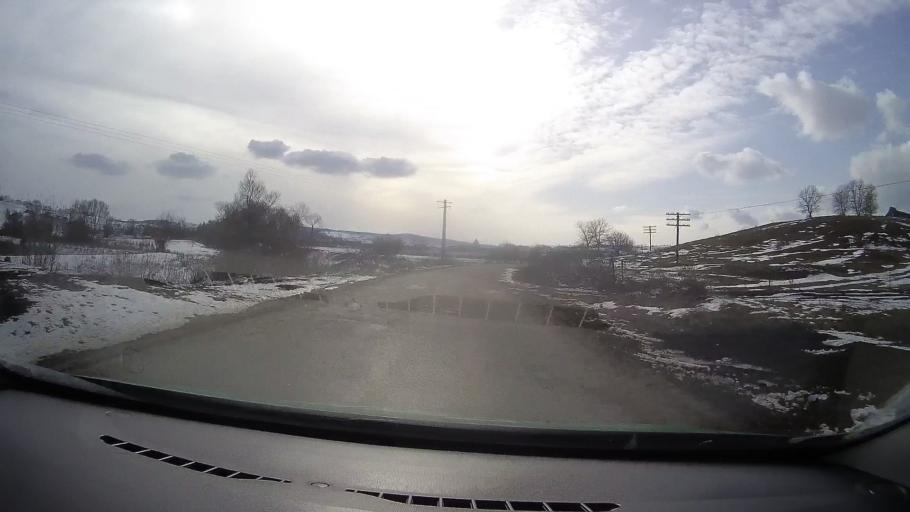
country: RO
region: Sibiu
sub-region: Comuna Bradeni
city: Bradeni
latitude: 46.0656
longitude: 24.7982
